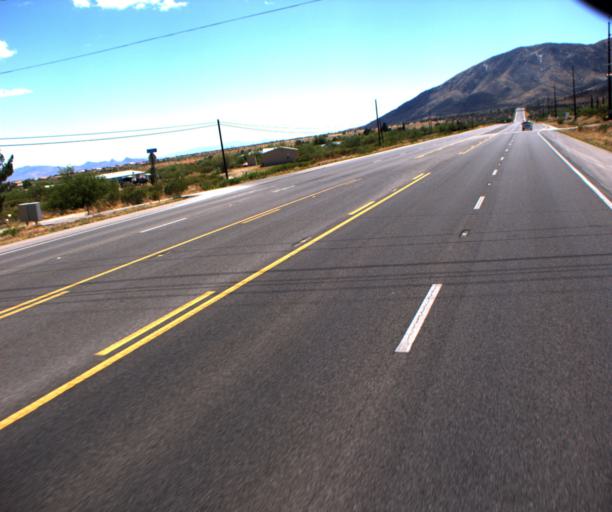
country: US
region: Arizona
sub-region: Cochise County
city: Sierra Vista Southeast
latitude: 31.4277
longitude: -110.2408
